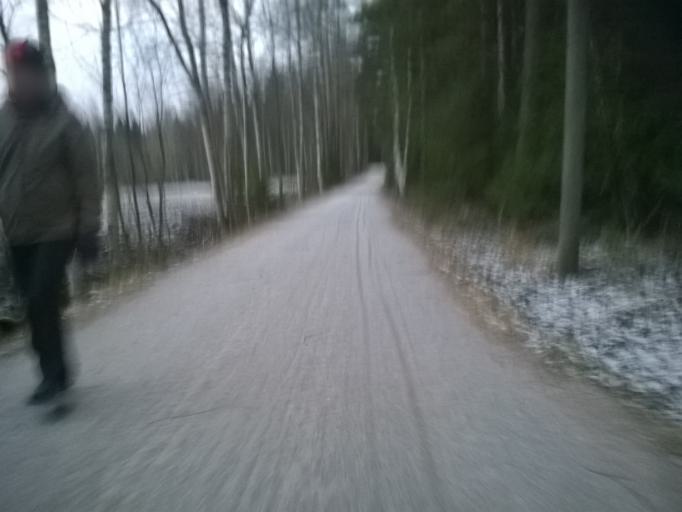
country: FI
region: Uusimaa
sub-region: Helsinki
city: Helsinki
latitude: 60.2498
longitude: 24.9096
